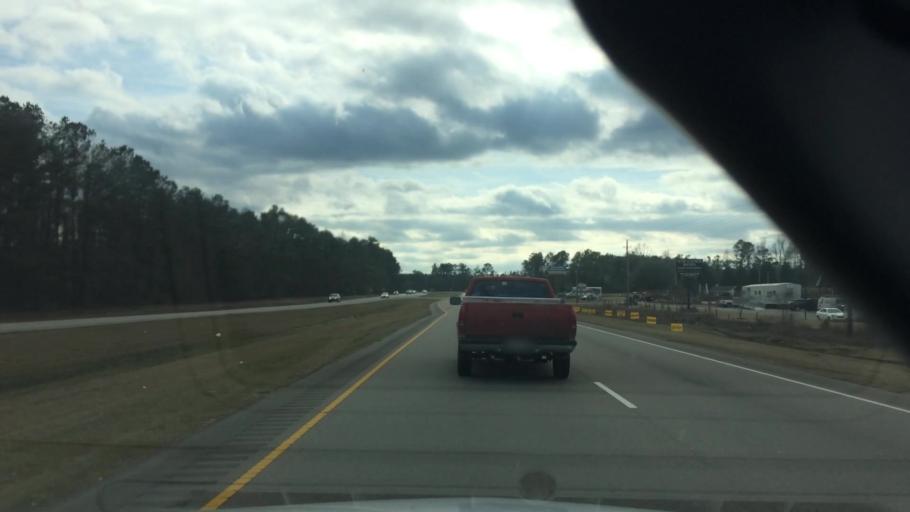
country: US
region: North Carolina
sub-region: Brunswick County
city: Bolivia
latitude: 34.1553
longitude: -78.0925
